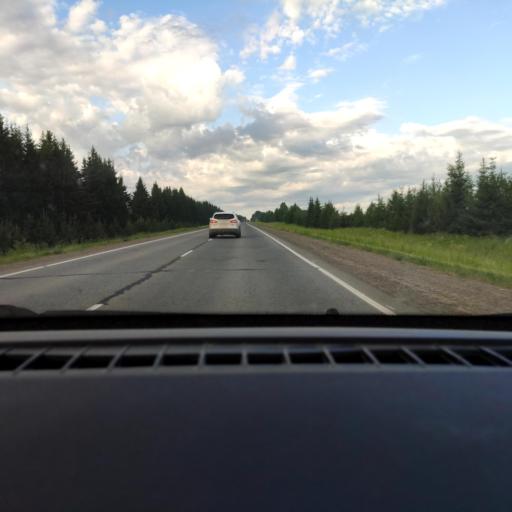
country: RU
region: Perm
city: Ocher
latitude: 57.4535
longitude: 54.4767
